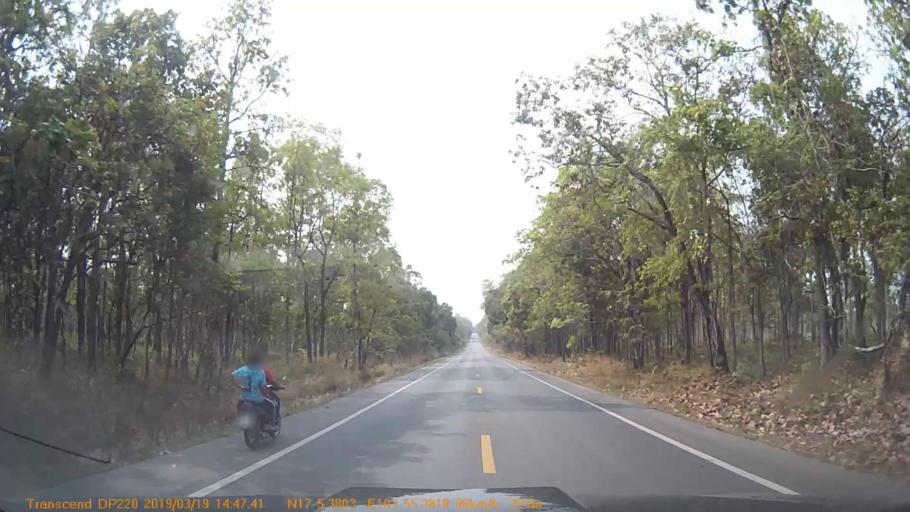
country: TH
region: Sakon Nakhon
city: Kut Bak
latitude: 17.0899
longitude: 103.9228
